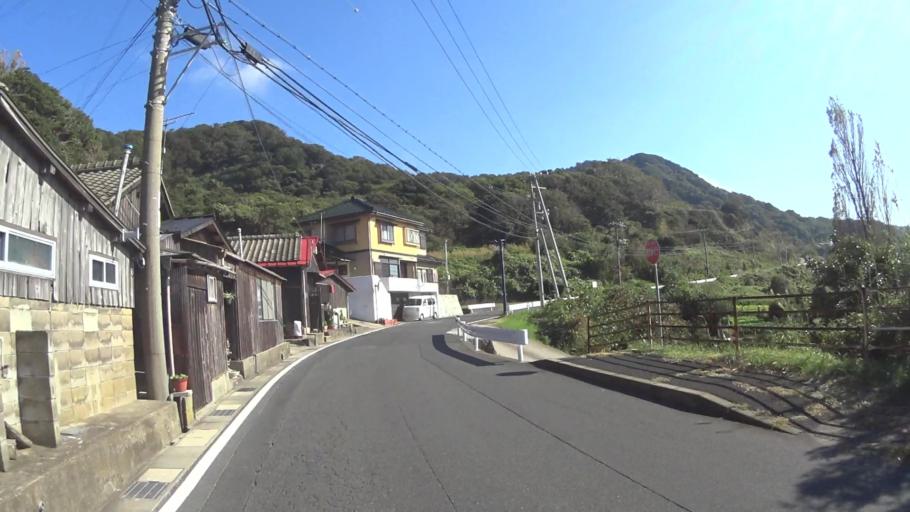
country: JP
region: Kyoto
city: Miyazu
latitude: 35.7331
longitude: 135.0879
